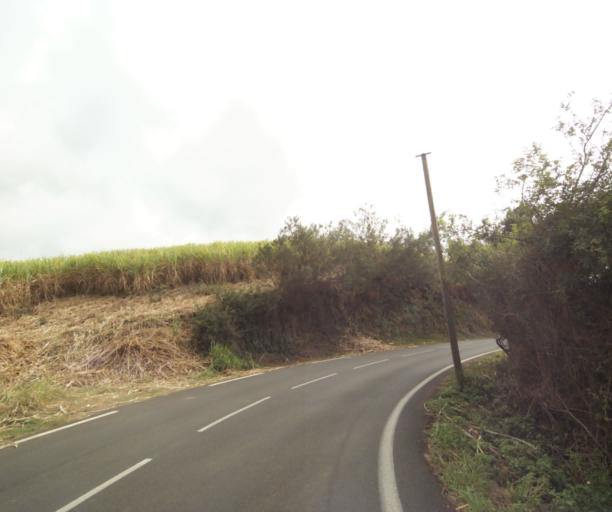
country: RE
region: Reunion
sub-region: Reunion
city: Saint-Paul
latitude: -21.0258
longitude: 55.3142
